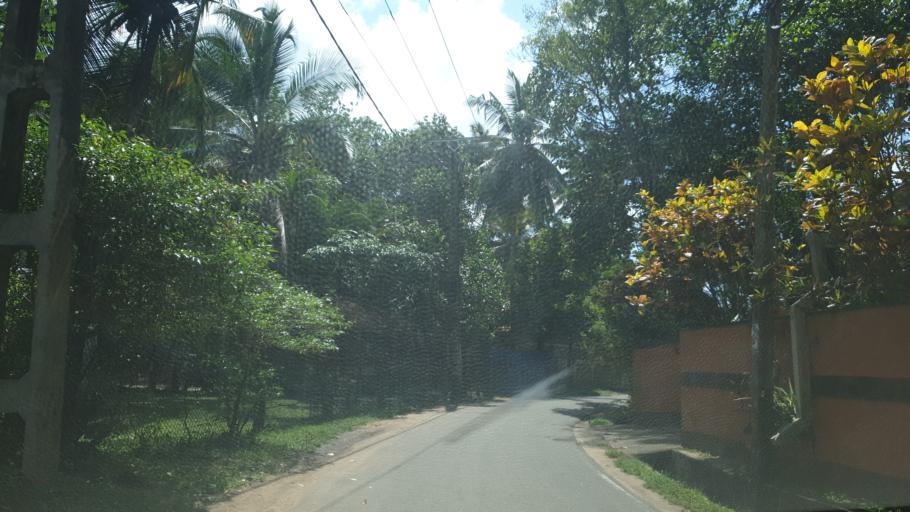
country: LK
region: Western
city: Panadura
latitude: 6.6847
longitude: 79.9305
